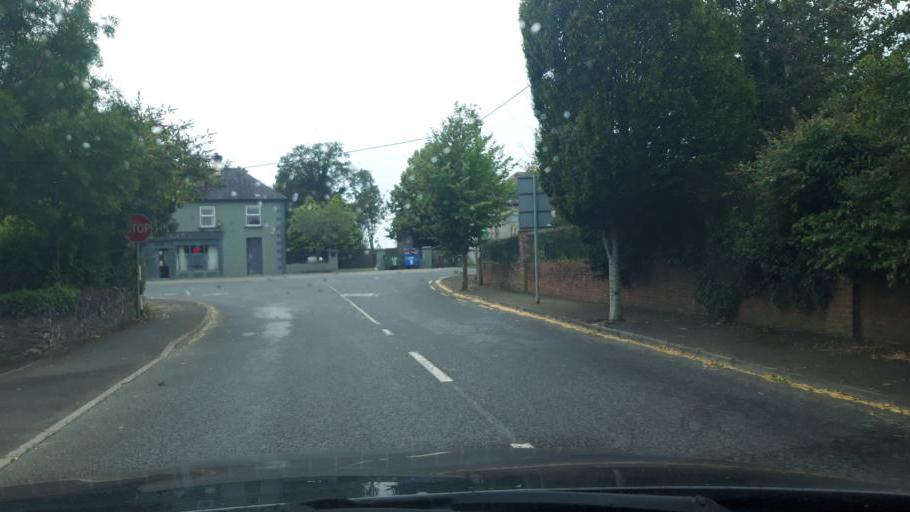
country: IE
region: Leinster
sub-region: Kildare
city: Monasterevin
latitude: 53.1051
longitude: -7.0152
